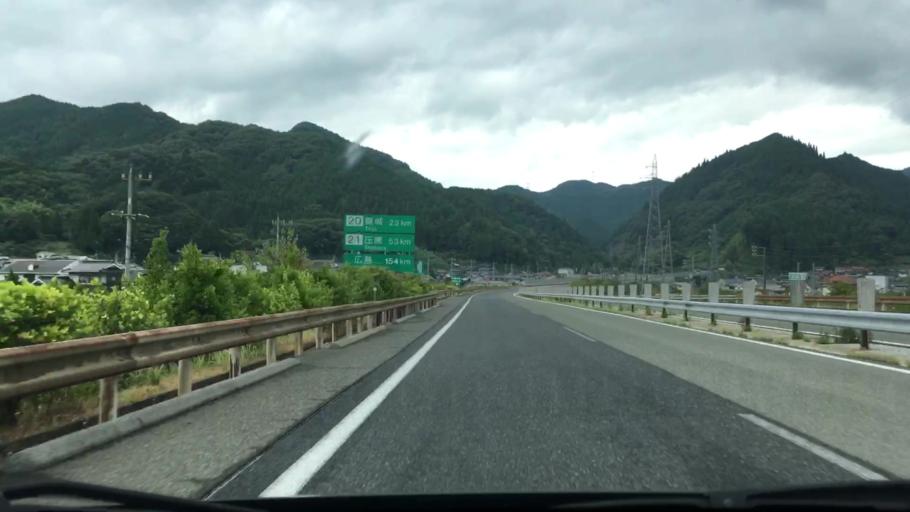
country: JP
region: Okayama
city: Niimi
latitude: 35.0071
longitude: 133.4382
